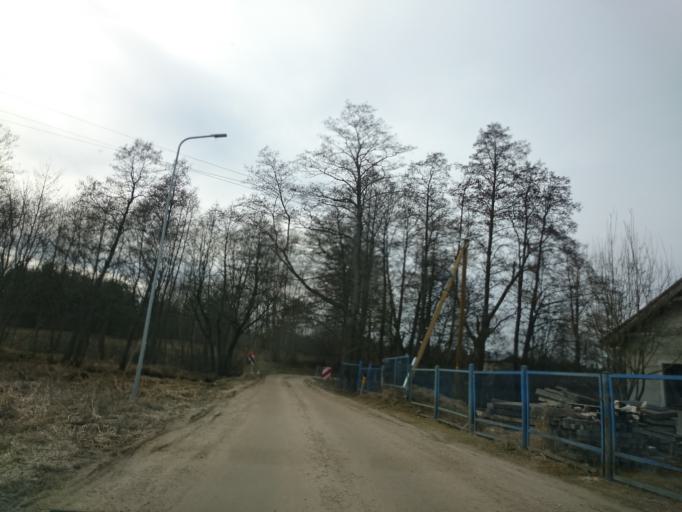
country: LV
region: Garkalne
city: Garkalne
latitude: 57.0165
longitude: 24.3922
